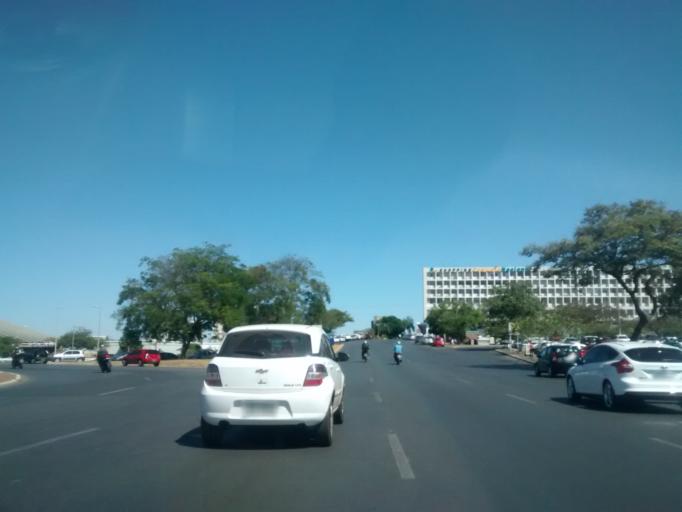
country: BR
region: Federal District
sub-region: Brasilia
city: Brasilia
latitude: -15.7885
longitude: -47.8818
